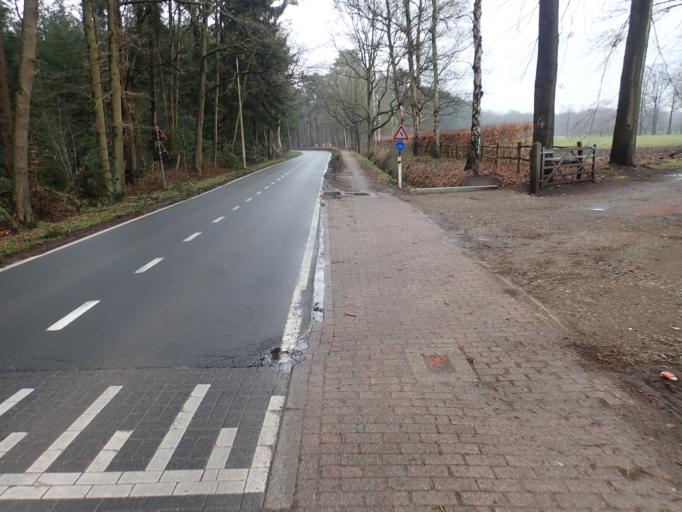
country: BE
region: Flanders
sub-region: Provincie Antwerpen
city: Kapellen
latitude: 51.3347
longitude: 4.4516
